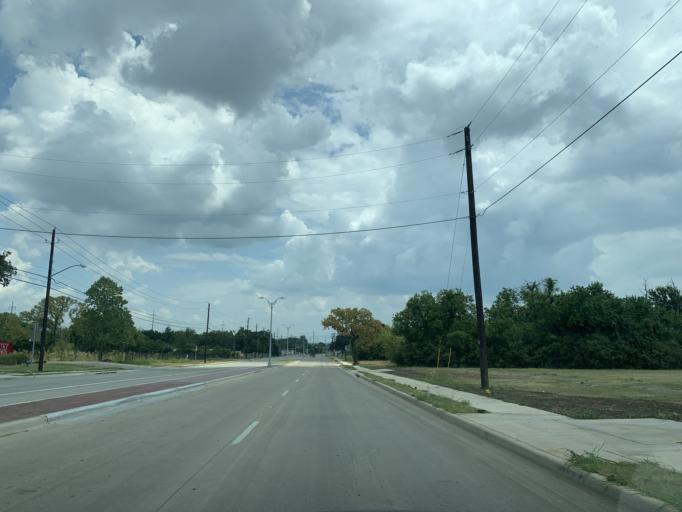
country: US
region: Texas
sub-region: Tarrant County
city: Forest Hill
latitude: 32.7311
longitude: -97.2496
